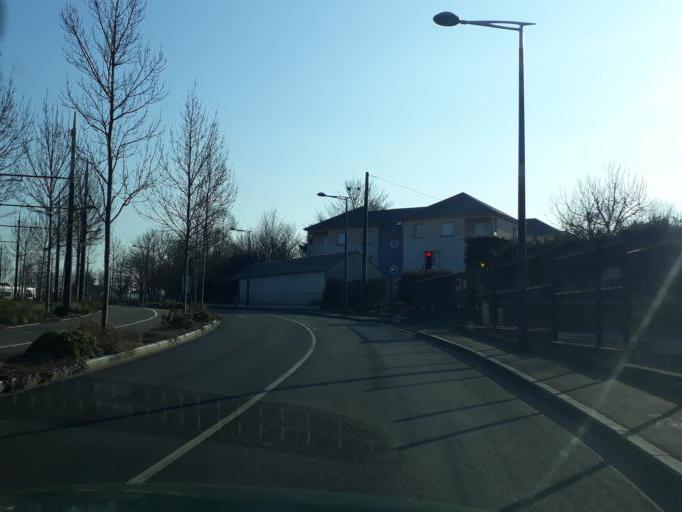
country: FR
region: Centre
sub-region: Departement du Loiret
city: Semoy
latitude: 47.9095
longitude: 1.9473
